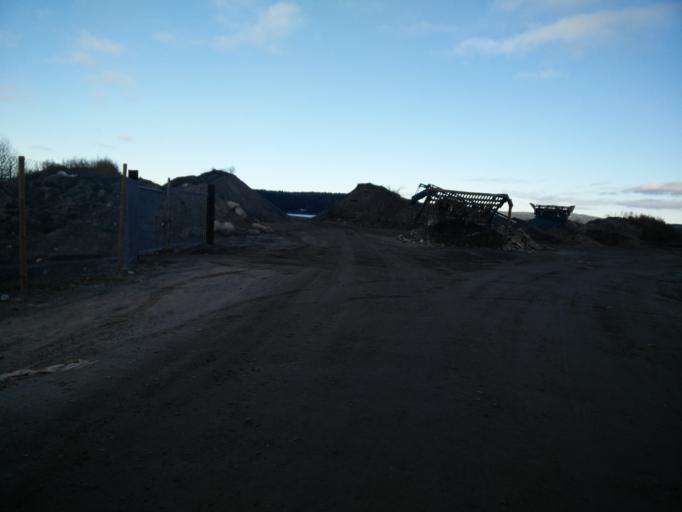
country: SE
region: Vaesternorrland
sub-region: Haernoesands Kommun
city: Haernoesand
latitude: 62.6435
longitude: 17.9556
